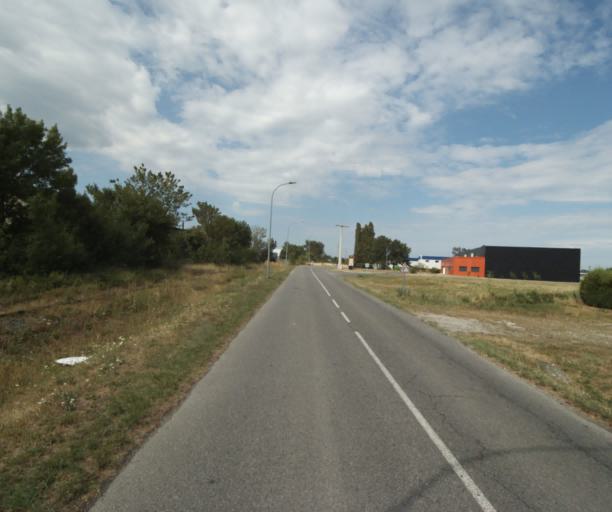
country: FR
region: Midi-Pyrenees
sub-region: Departement de la Haute-Garonne
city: Revel
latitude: 43.4546
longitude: 1.9903
